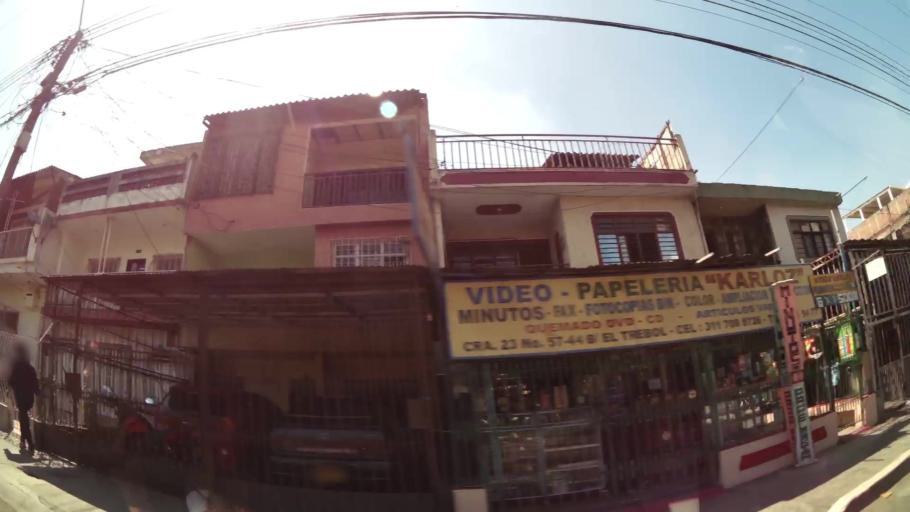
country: CO
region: Valle del Cauca
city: Cali
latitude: 3.4421
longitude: -76.4953
